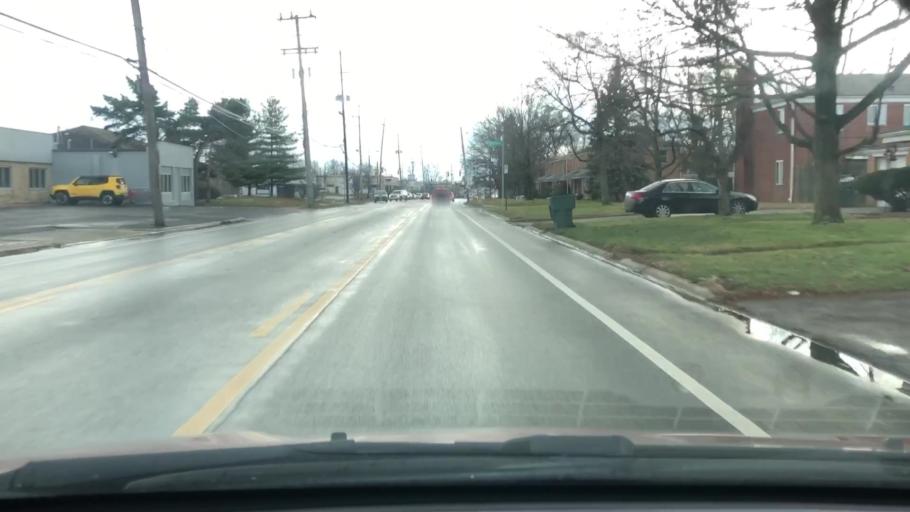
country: US
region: Ohio
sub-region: Franklin County
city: Worthington
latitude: 40.0501
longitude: -83.0000
